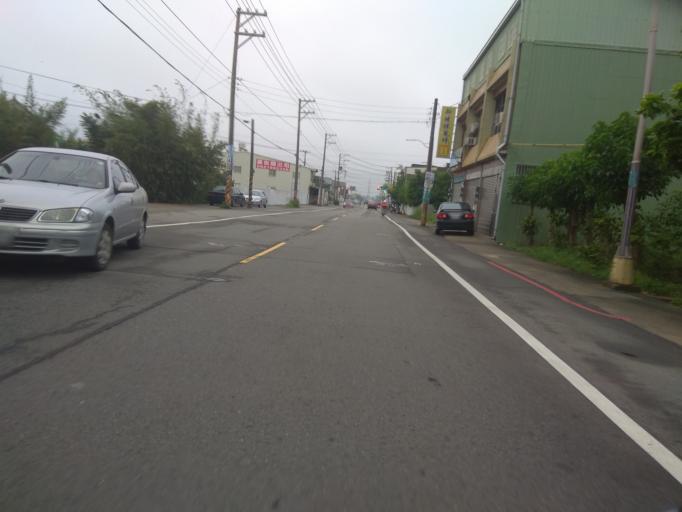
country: TW
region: Taiwan
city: Taoyuan City
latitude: 25.0149
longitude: 121.1321
